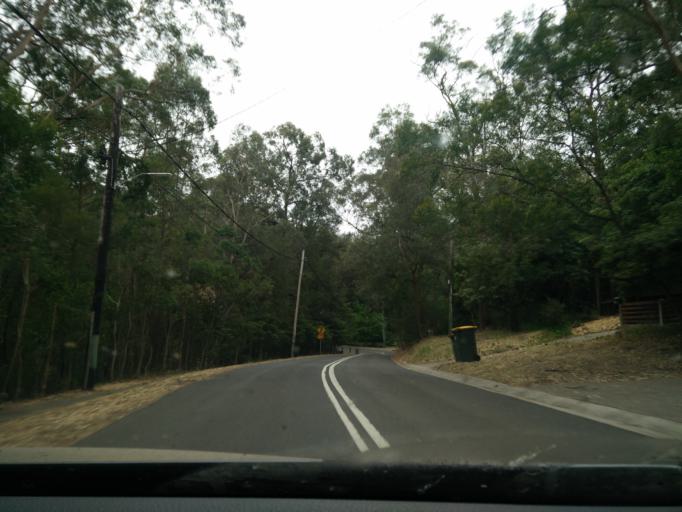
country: AU
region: New South Wales
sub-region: Blue Mountains Municipality
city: Glenbrook
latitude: -33.7715
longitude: 150.6236
